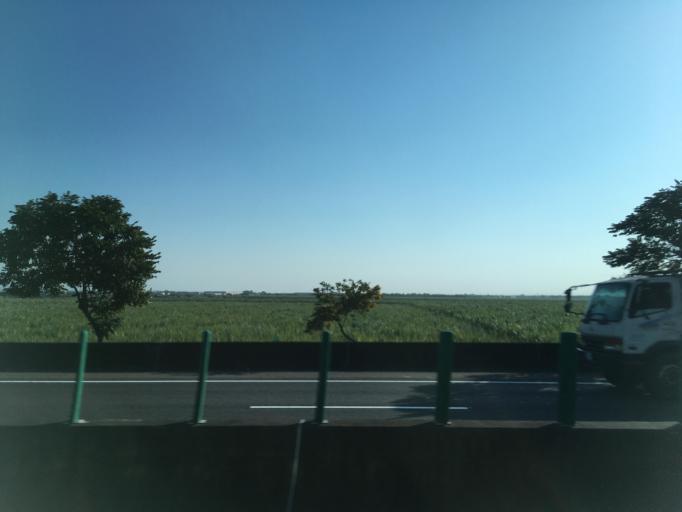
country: TW
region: Taiwan
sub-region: Chiayi
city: Taibao
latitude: 23.4285
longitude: 120.3302
